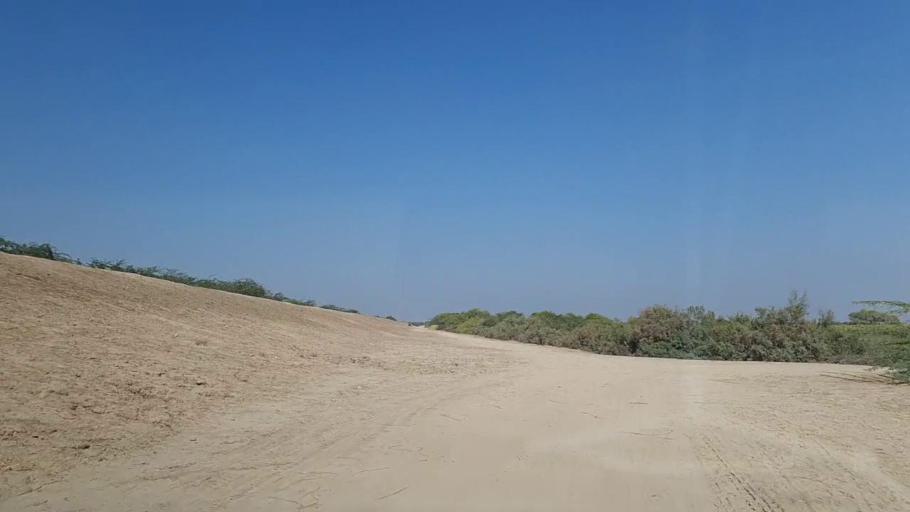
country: PK
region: Sindh
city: Chuhar Jamali
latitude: 24.4737
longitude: 68.0091
